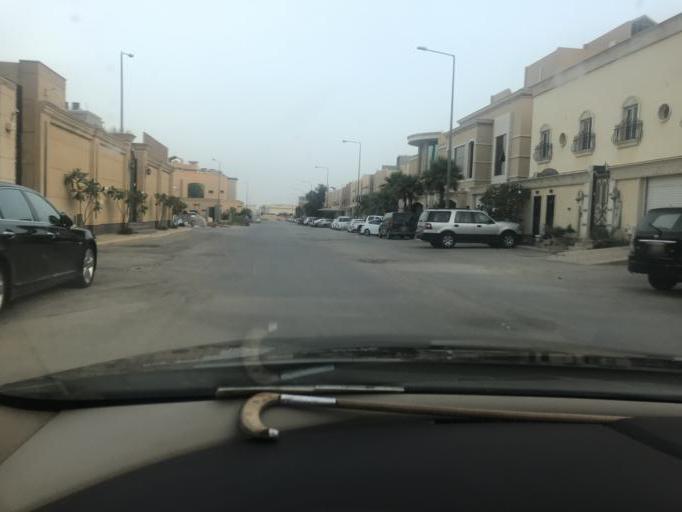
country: SA
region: Ar Riyad
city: Riyadh
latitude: 24.7296
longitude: 46.7448
